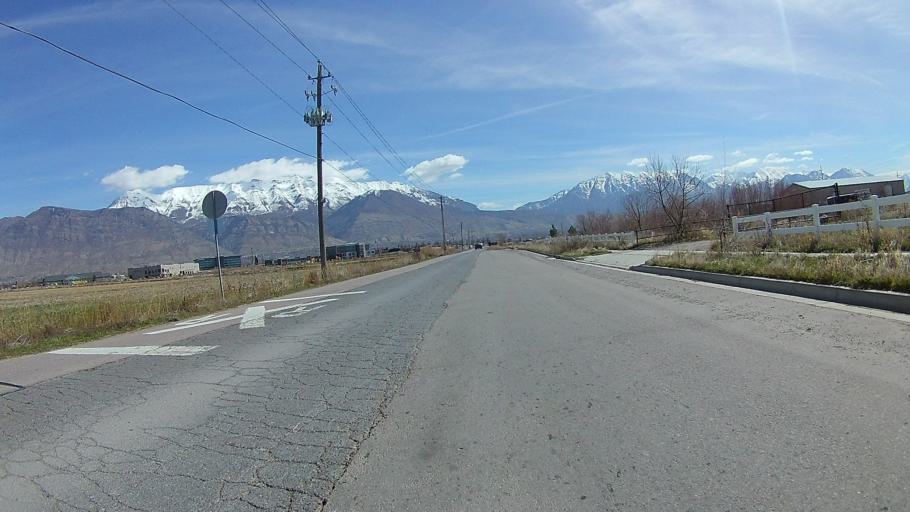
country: US
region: Utah
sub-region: Utah County
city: American Fork
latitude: 40.3476
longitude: -111.7787
